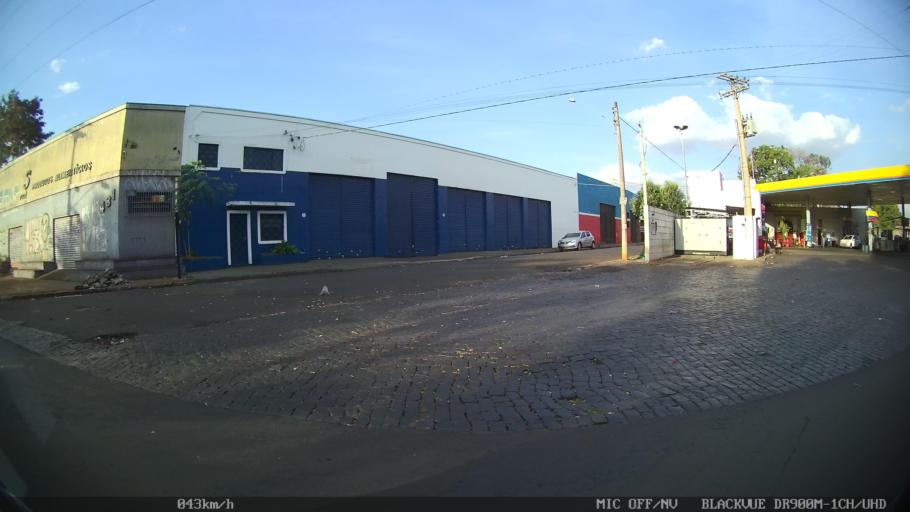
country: BR
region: Sao Paulo
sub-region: Ribeirao Preto
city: Ribeirao Preto
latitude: -21.1241
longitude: -47.7857
